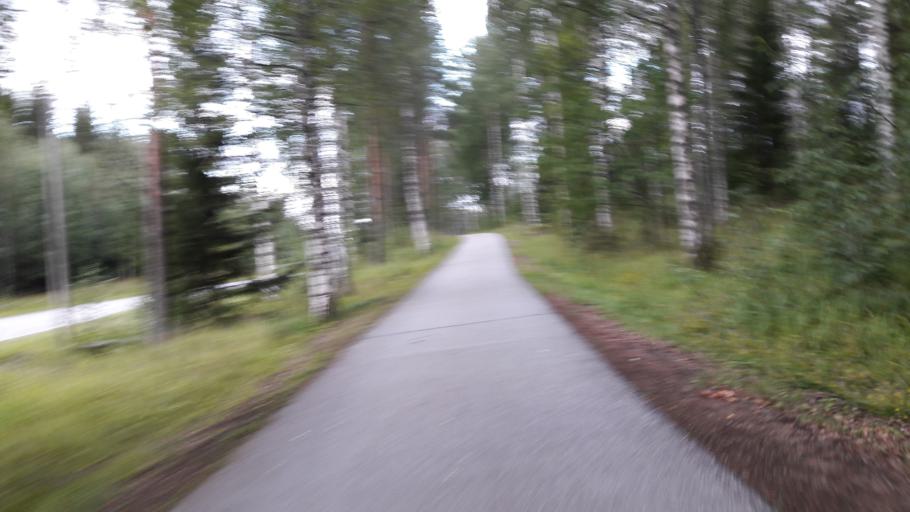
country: FI
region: North Karelia
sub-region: Joensuu
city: Joensuu
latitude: 62.5268
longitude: 29.8546
